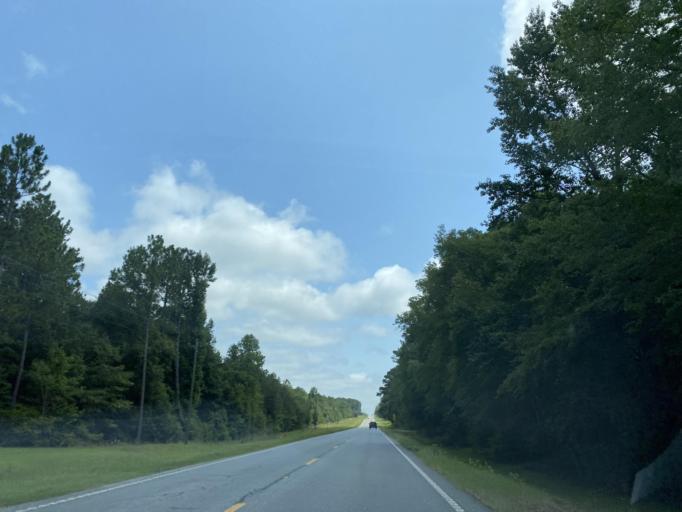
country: US
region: Georgia
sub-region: Telfair County
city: McRae
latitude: 32.1013
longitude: -82.8404
